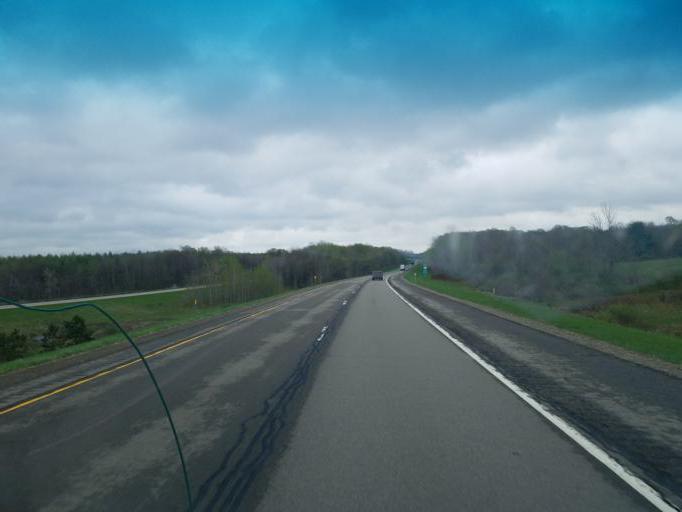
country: US
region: New York
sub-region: Chautauqua County
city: Clymer
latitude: 42.1447
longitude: -79.7015
